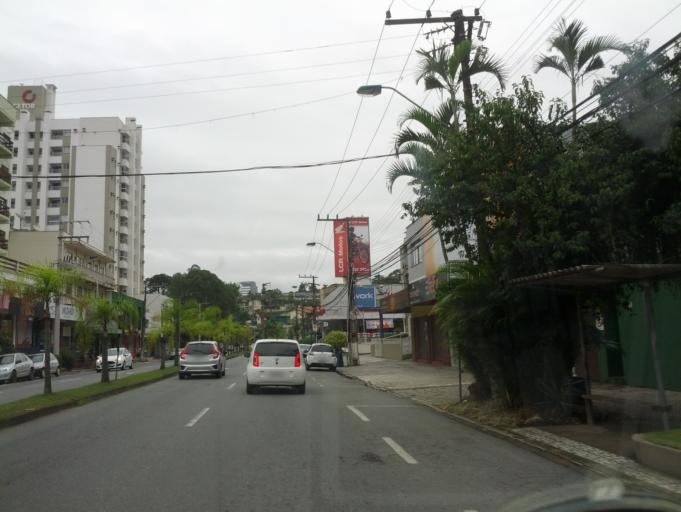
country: BR
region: Santa Catarina
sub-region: Blumenau
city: Blumenau
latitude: -26.9082
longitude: -49.0803
